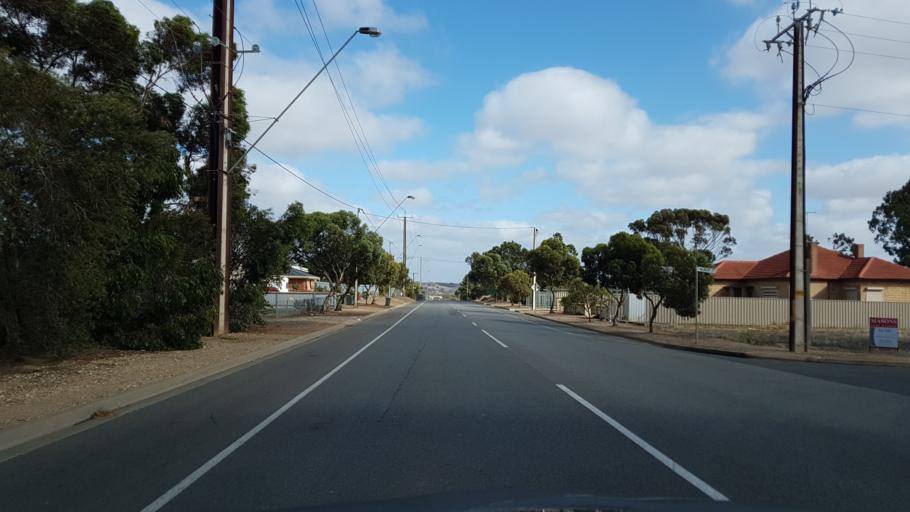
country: AU
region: South Australia
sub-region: Murray Bridge
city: Murray Bridge
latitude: -35.1217
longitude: 139.2533
